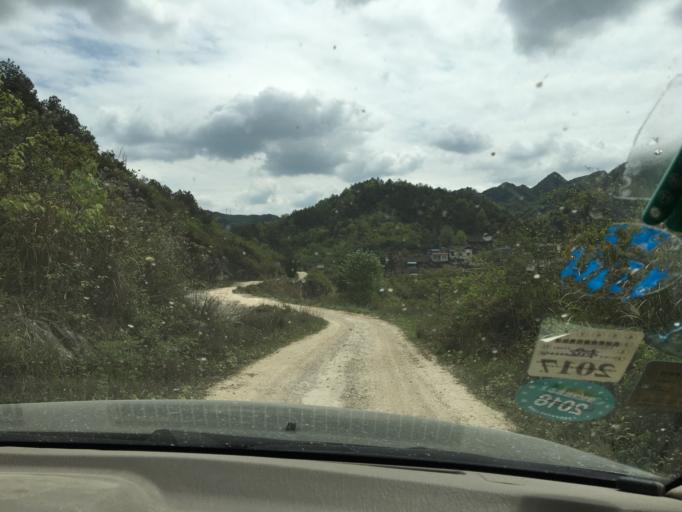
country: CN
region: Guizhou Sheng
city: Kuanping
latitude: 28.0207
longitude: 108.0731
